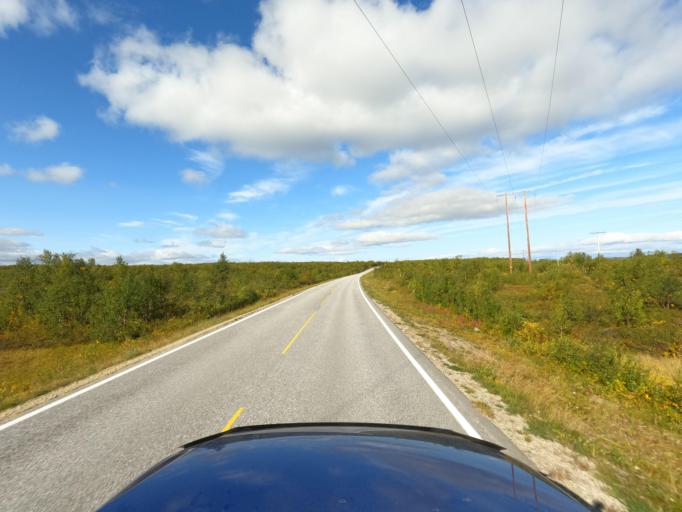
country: NO
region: Finnmark Fylke
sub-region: Karasjok
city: Karasjohka
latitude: 69.6117
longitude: 25.3069
